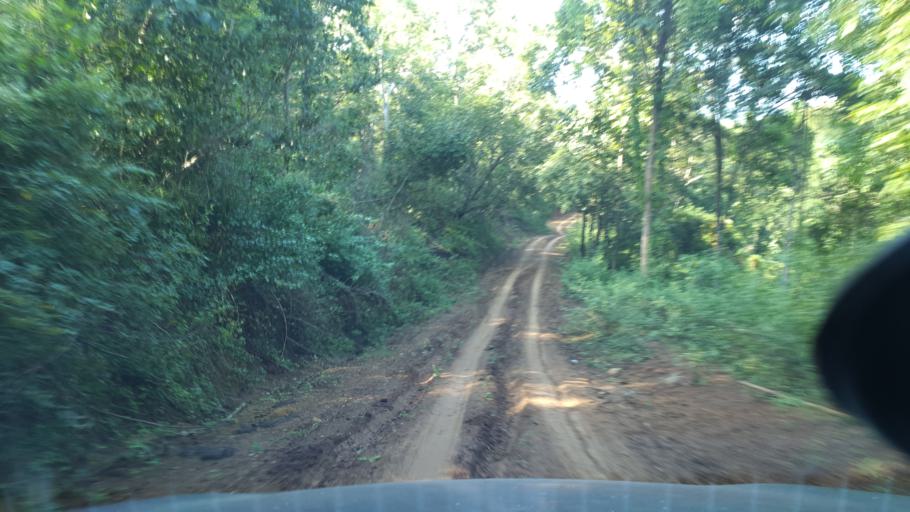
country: TH
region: Chiang Mai
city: Wiang Haeng
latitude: 19.3615
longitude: 98.7179
